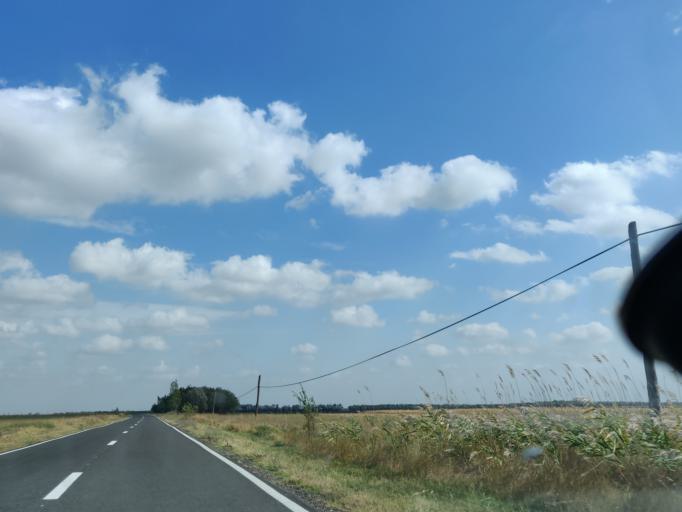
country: RO
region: Vrancea
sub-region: Comuna Maicanesti
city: Ramniceni
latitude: 45.4740
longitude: 27.4321
